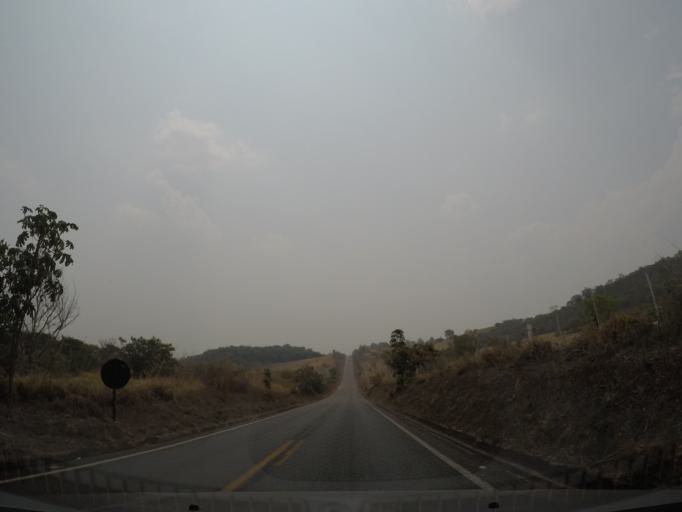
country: BR
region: Goias
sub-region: Pirenopolis
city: Pirenopolis
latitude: -15.9221
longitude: -48.8542
